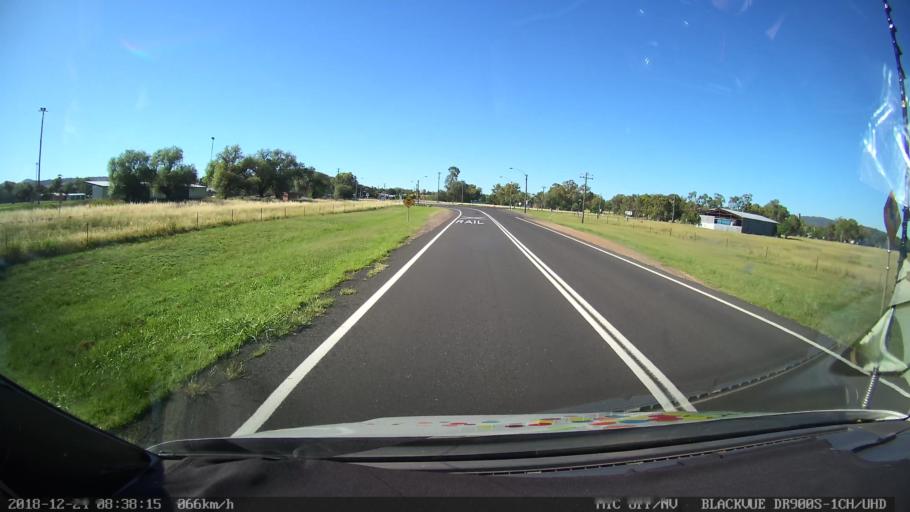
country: AU
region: New South Wales
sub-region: Liverpool Plains
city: Quirindi
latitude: -31.3394
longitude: 150.6476
